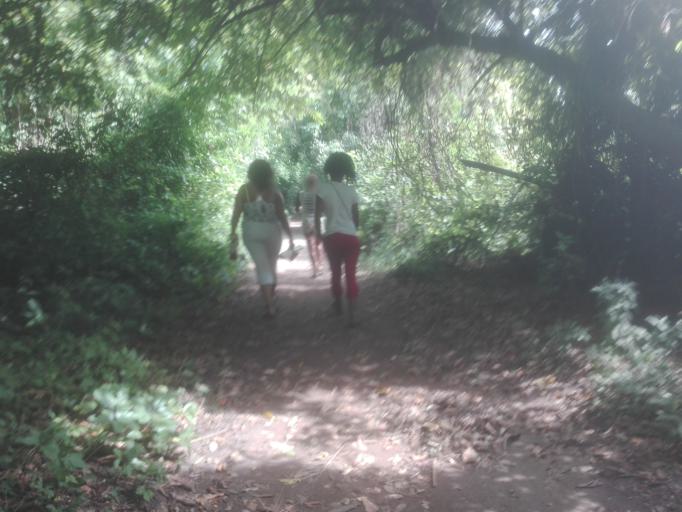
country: CO
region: Bolivar
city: Turbana
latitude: 10.1791
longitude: -75.7397
